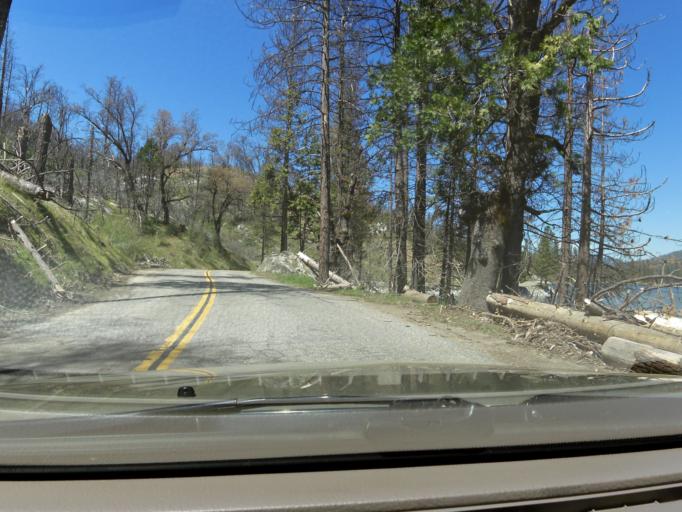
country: US
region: California
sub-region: Madera County
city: Oakhurst
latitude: 37.3175
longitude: -119.5749
